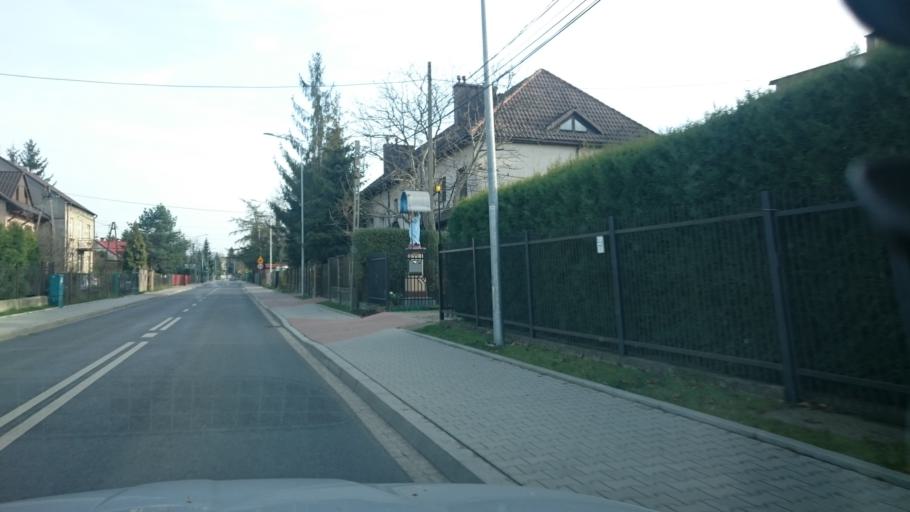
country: PL
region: Lesser Poland Voivodeship
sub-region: Powiat wielicki
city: Czarnochowice
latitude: 50.0202
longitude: 20.0209
